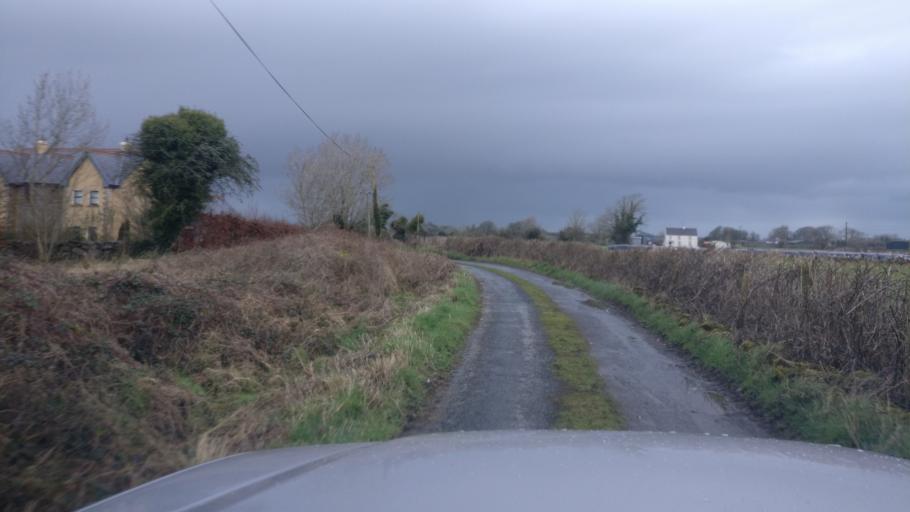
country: IE
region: Connaught
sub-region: County Galway
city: Loughrea
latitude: 53.1998
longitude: -8.6130
